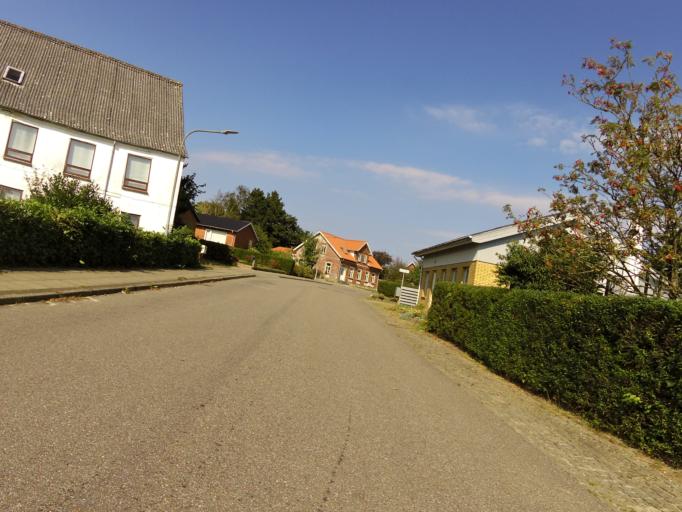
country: DK
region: South Denmark
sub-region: Vejen Kommune
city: Vejen
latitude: 55.4228
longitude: 9.1536
